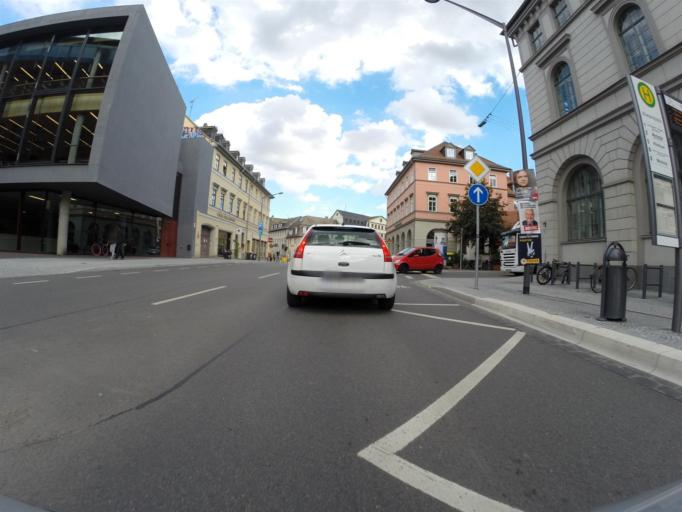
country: DE
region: Thuringia
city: Weimar
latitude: 50.9772
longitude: 11.3270
